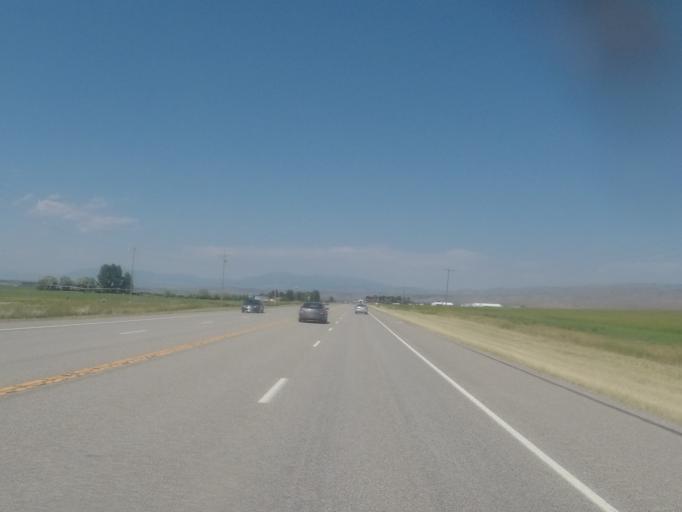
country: US
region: Montana
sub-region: Broadwater County
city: Townsend
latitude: 46.1307
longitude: -111.4870
